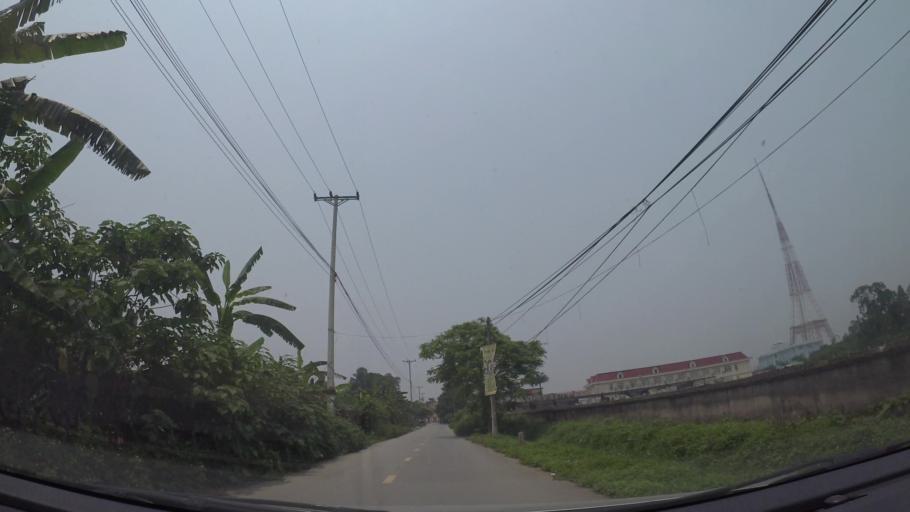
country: VN
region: Ha Noi
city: Ha Dong
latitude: 20.9980
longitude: 105.7657
